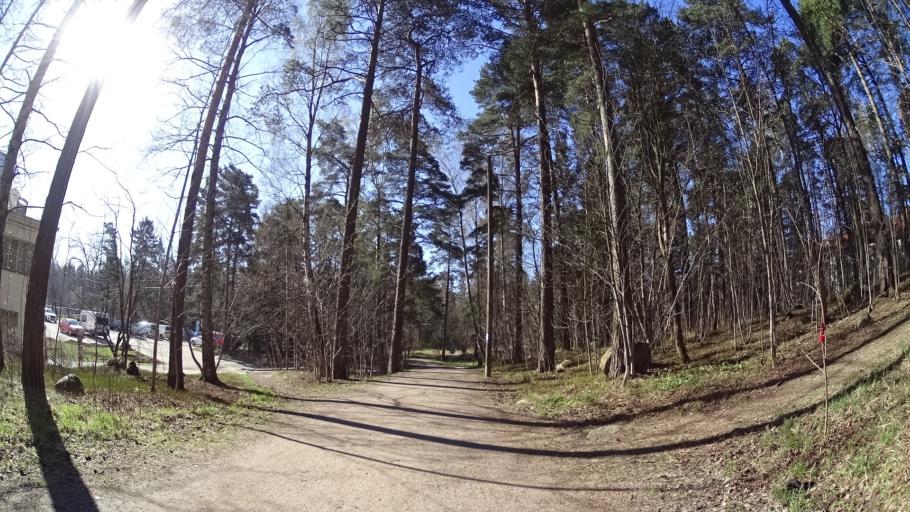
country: FI
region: Uusimaa
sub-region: Helsinki
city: Helsinki
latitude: 60.1985
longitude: 24.9094
